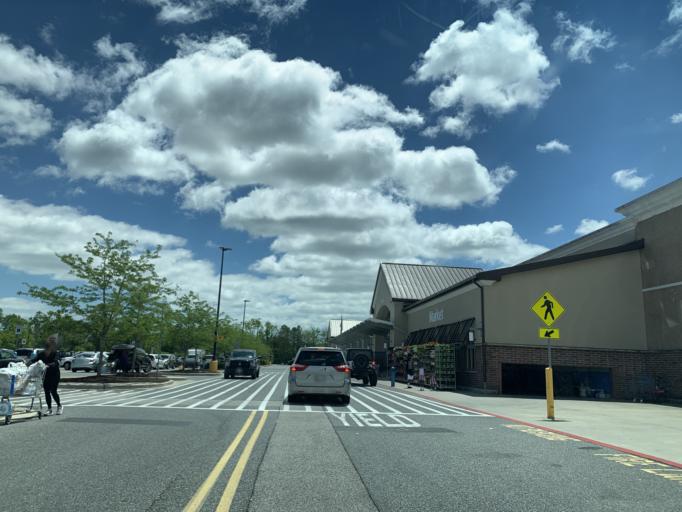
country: US
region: Maryland
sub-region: Worcester County
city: Ocean Pines
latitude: 38.3402
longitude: -75.1632
